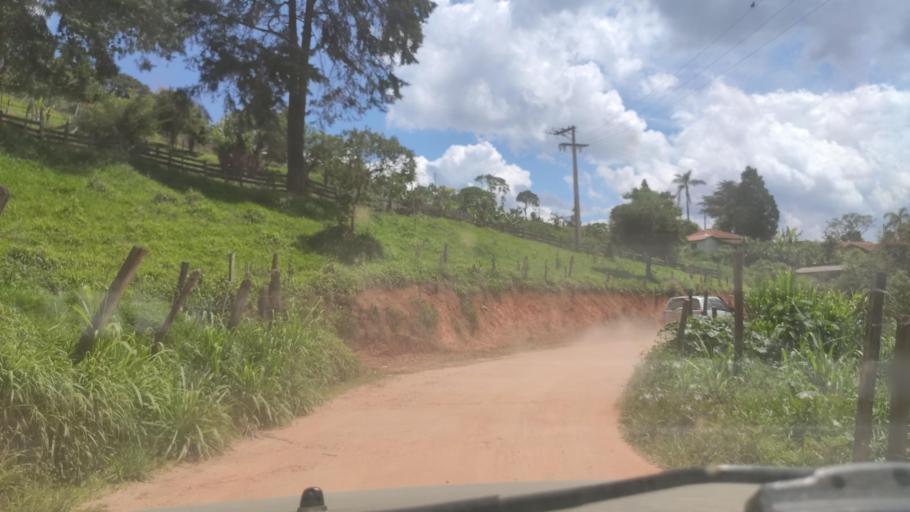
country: BR
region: Minas Gerais
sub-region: Cambui
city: Cambui
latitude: -22.7026
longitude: -46.0130
